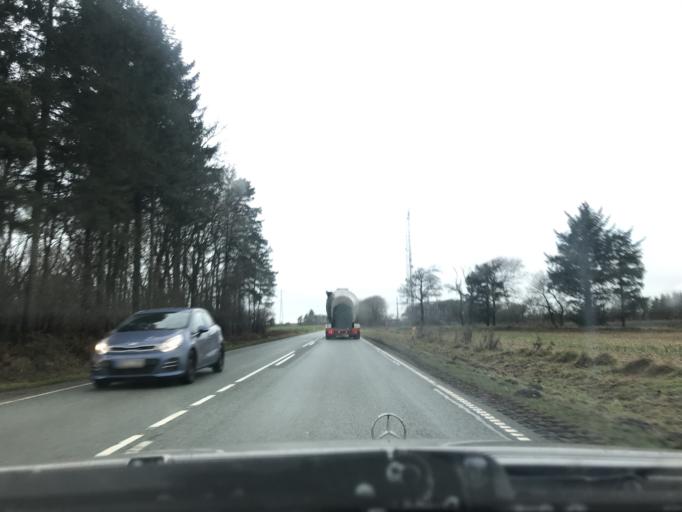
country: DK
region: South Denmark
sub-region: Haderslev Kommune
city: Gram
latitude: 55.2511
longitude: 8.9196
